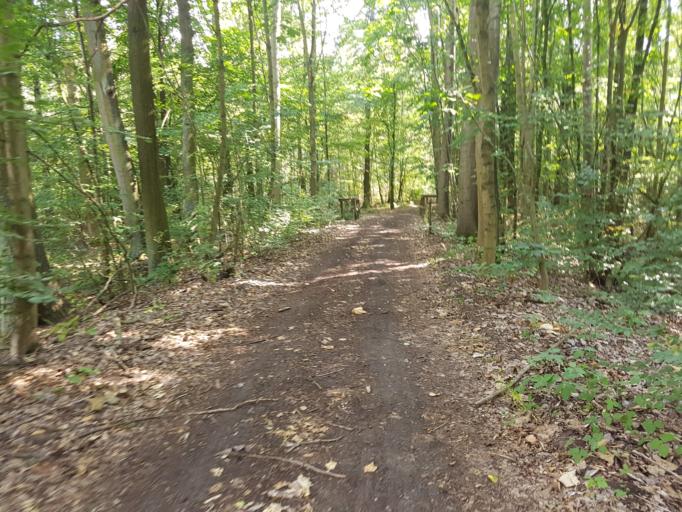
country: DE
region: Brandenburg
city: Calau
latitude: 51.7674
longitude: 13.9523
